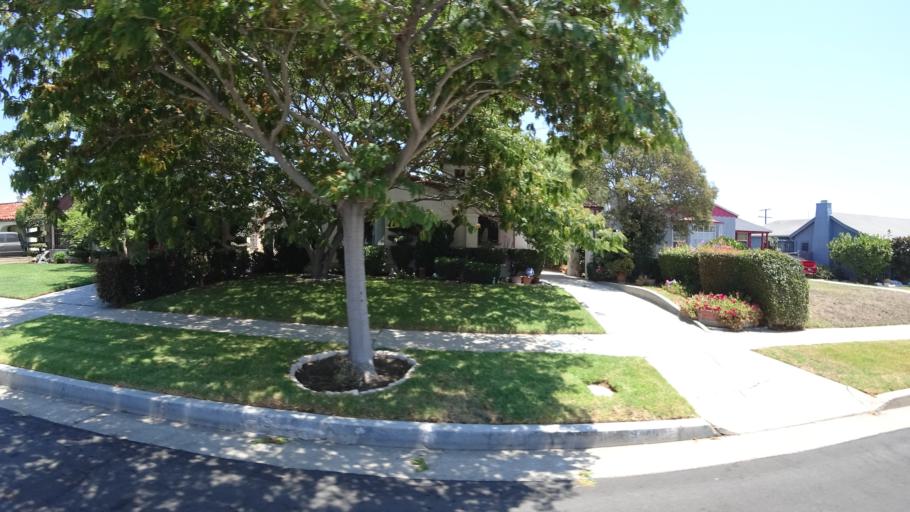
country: US
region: California
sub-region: Los Angeles County
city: Westmont
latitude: 33.9497
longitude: -118.3057
